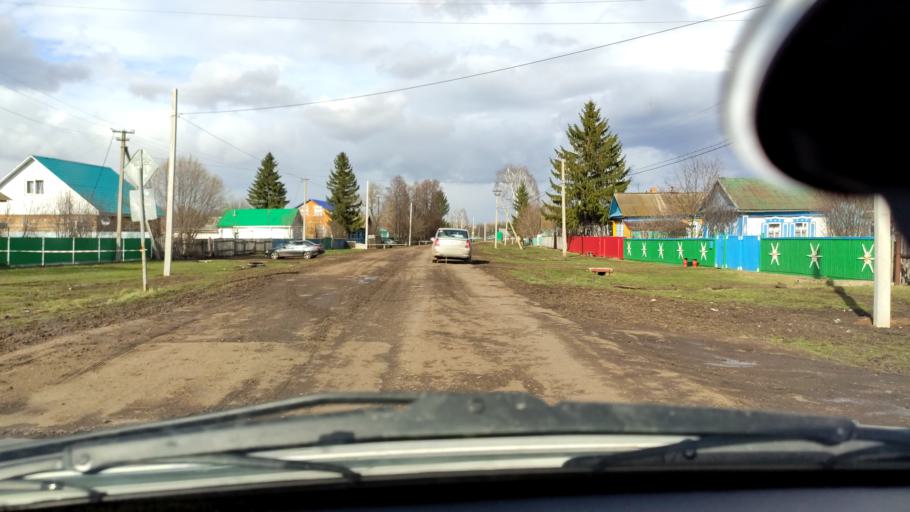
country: RU
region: Bashkortostan
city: Buzdyak
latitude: 54.7651
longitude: 54.6185
